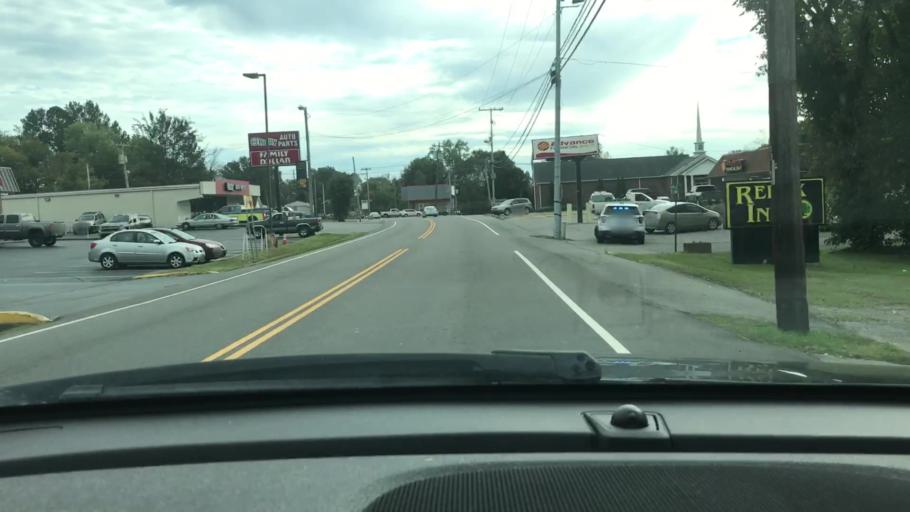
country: US
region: Tennessee
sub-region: Cheatham County
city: Ashland City
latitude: 36.2670
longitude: -87.0591
